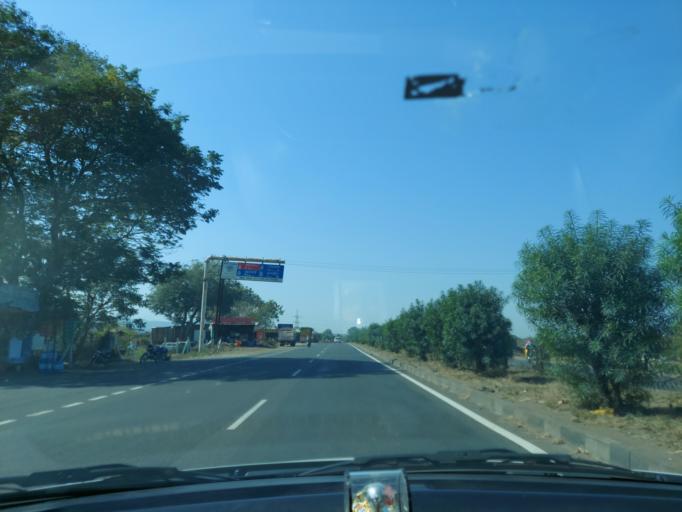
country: IN
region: Madhya Pradesh
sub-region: Indore
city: Manpur
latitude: 22.4262
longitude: 75.6107
